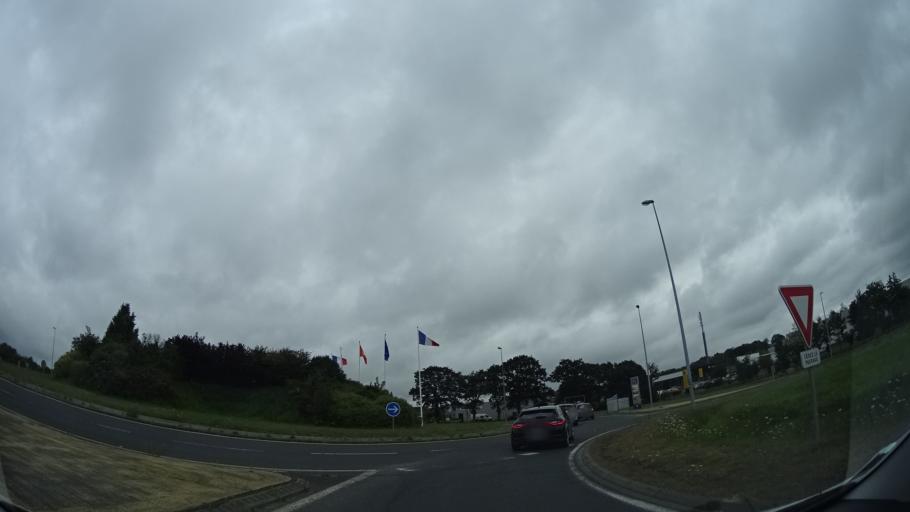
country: FR
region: Lower Normandy
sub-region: Departement de la Manche
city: La Haye-du-Puits
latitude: 49.2784
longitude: -1.5407
